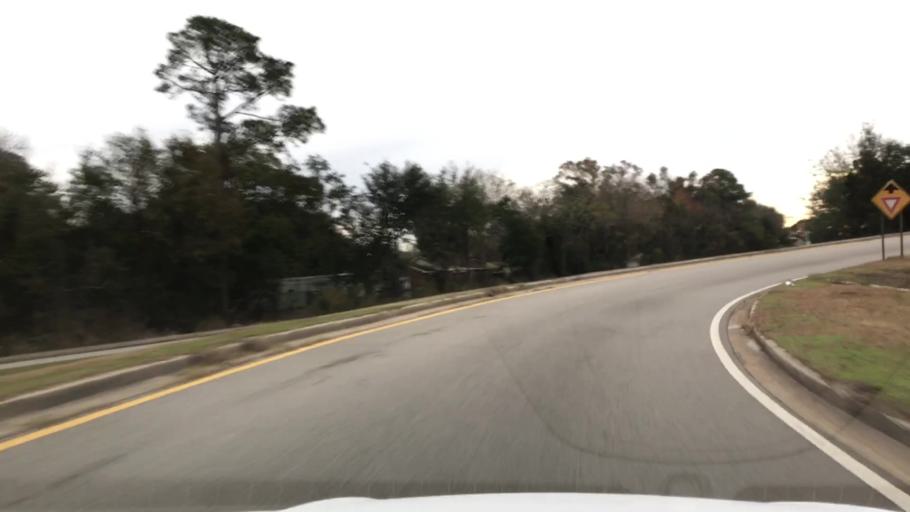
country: US
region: South Carolina
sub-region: Charleston County
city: North Charleston
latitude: 32.8444
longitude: -79.9792
